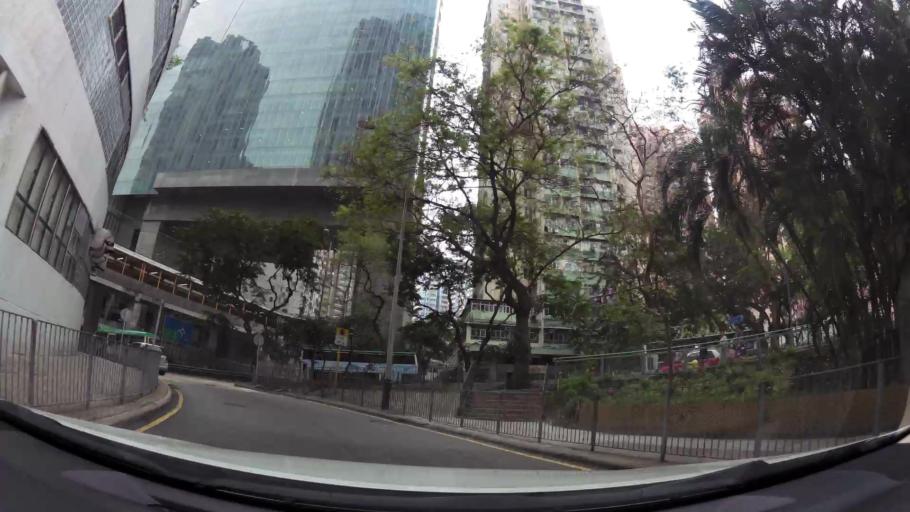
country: HK
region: Wanchai
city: Wan Chai
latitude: 22.2639
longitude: 114.2361
